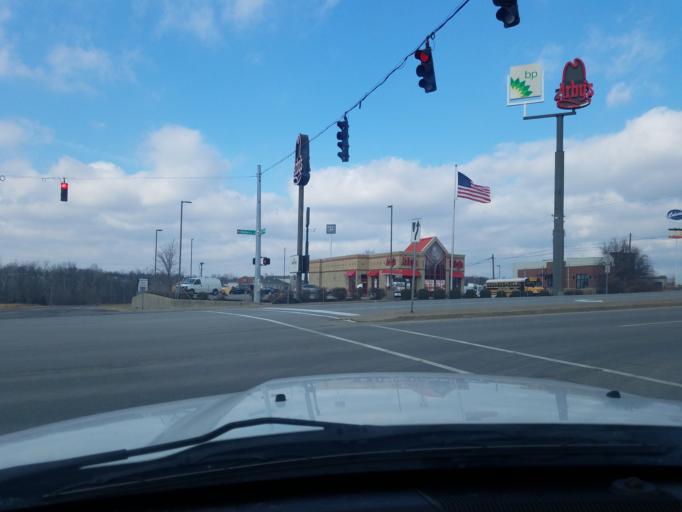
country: US
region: Kentucky
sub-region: Hardin County
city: Elizabethtown
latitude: 37.7124
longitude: -85.8318
